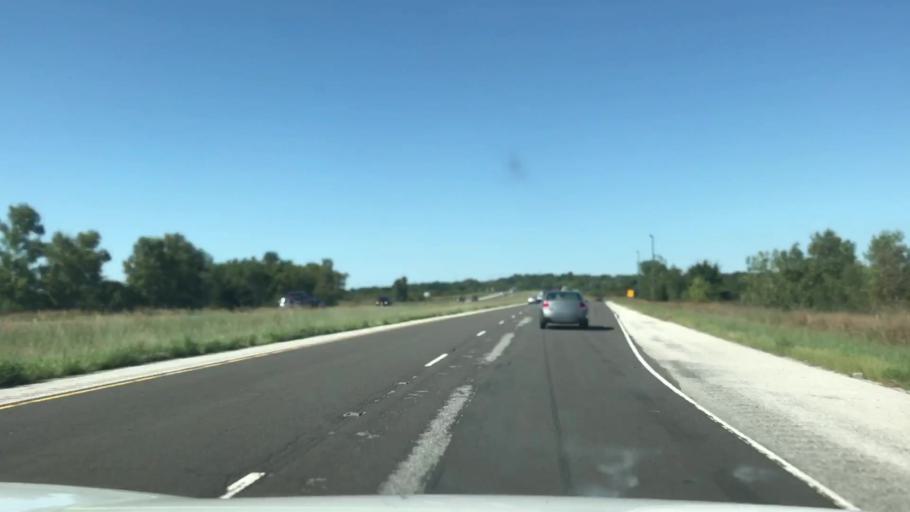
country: US
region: Illinois
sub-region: Madison County
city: South Roxana
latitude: 38.8268
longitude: -90.0435
